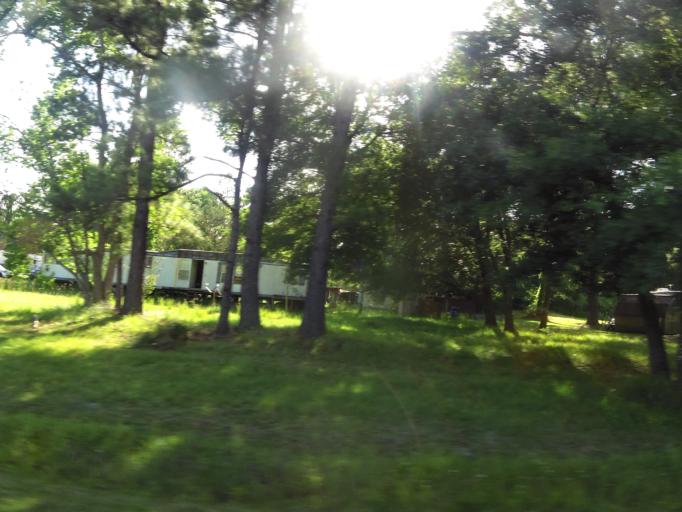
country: US
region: Florida
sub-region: Nassau County
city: Nassau Village-Ratliff
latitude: 30.5180
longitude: -81.7796
